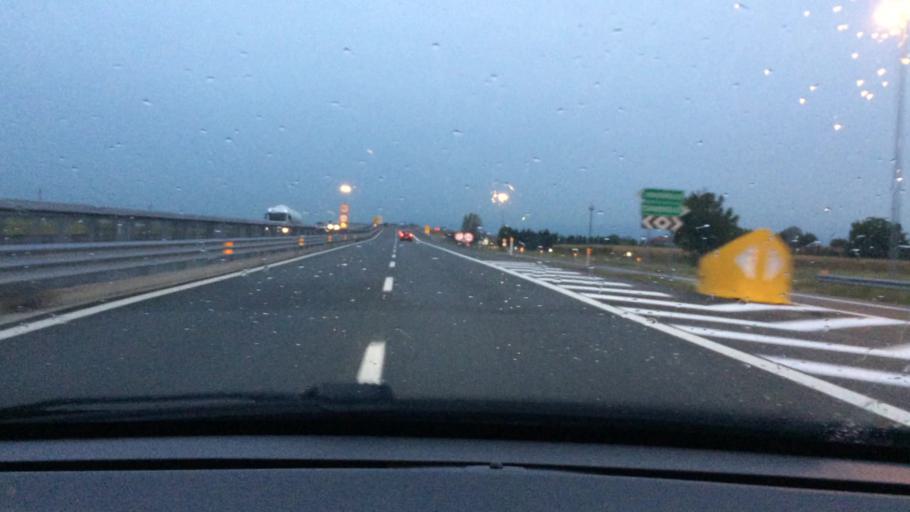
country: IT
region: Piedmont
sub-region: Provincia di Torino
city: Orbassano
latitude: 44.9846
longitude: 7.5550
